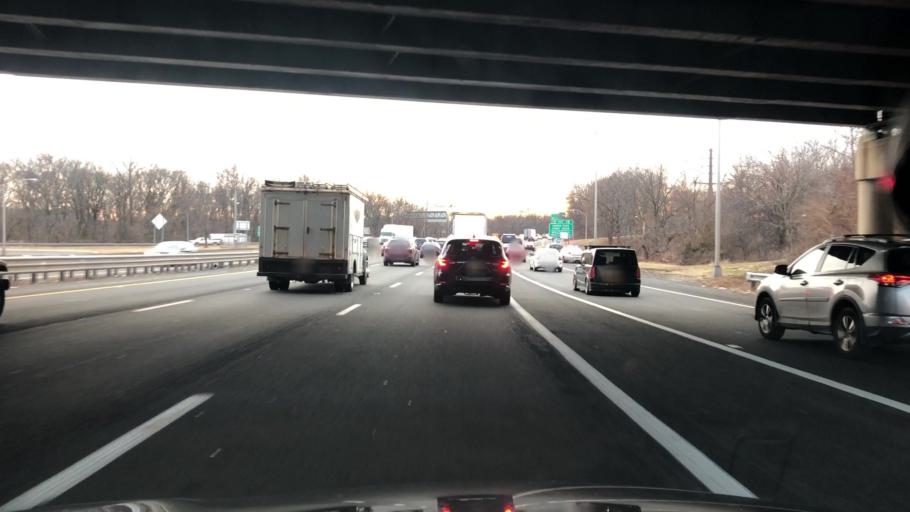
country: US
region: New Jersey
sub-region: Somerset County
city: South Bound Brook
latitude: 40.5414
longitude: -74.5069
